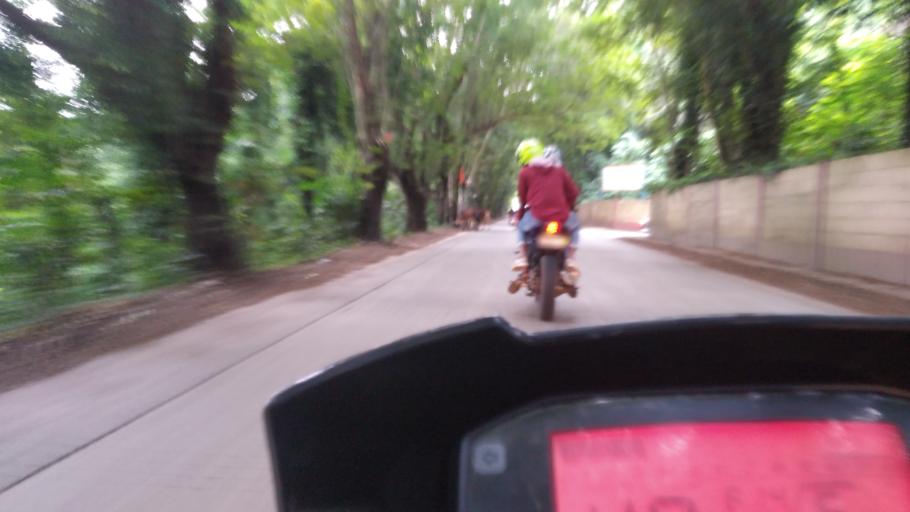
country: IN
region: Kerala
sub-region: Ernakulam
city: Aluva
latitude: 10.0491
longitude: 76.3402
